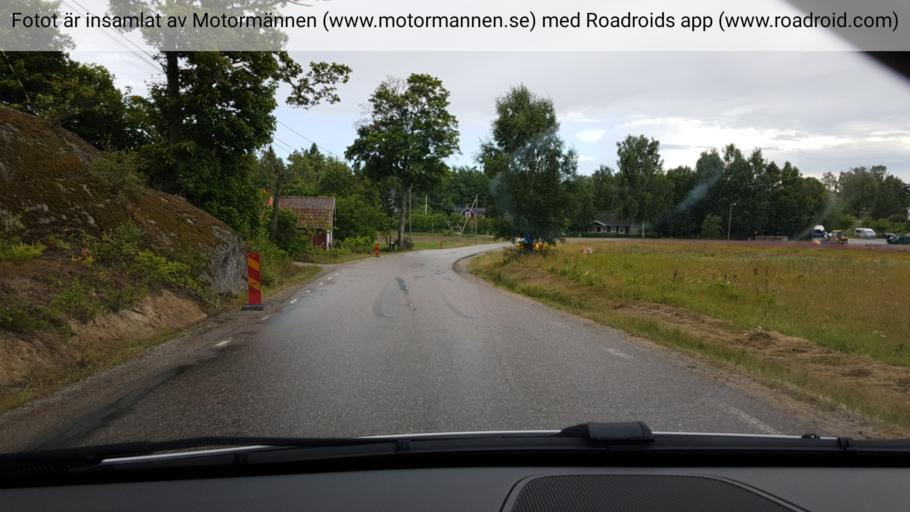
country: SE
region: Stockholm
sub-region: Nynashamns Kommun
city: Osmo
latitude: 59.0551
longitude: 17.8711
